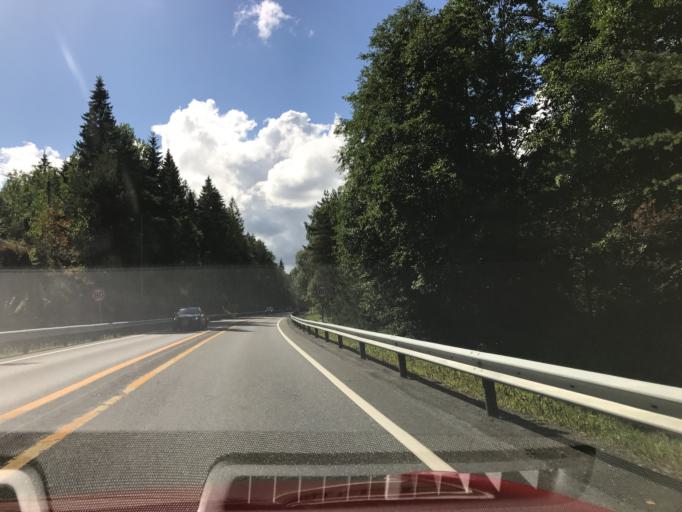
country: NO
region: Telemark
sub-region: Kragero
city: Kragero
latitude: 58.9627
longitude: 9.4736
